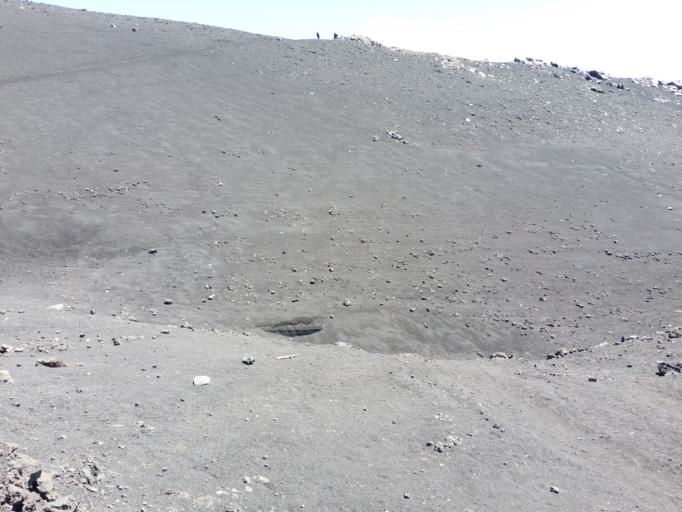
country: IT
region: Sicily
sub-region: Catania
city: Ragalna
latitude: 37.7186
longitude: 15.0005
